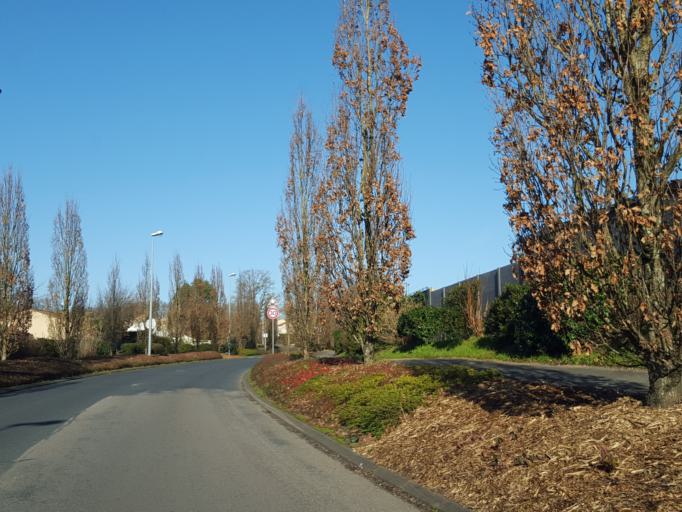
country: FR
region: Pays de la Loire
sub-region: Departement de la Vendee
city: La Roche-sur-Yon
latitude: 46.6606
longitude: -1.4542
